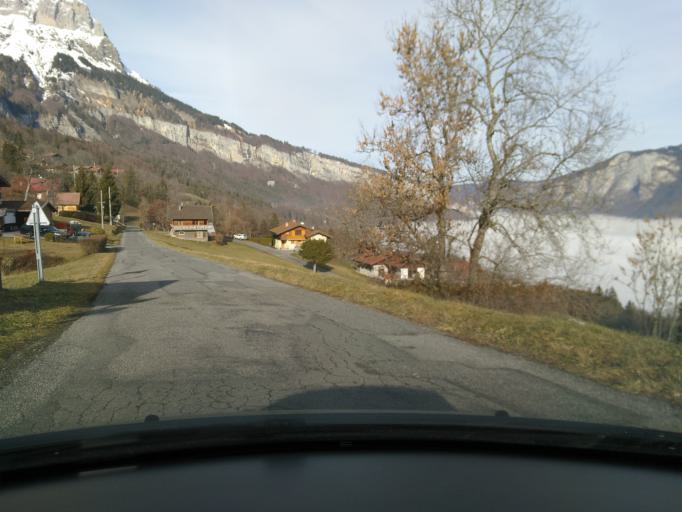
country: FR
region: Rhone-Alpes
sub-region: Departement de la Haute-Savoie
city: Sallanches
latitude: 45.9535
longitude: 6.6154
